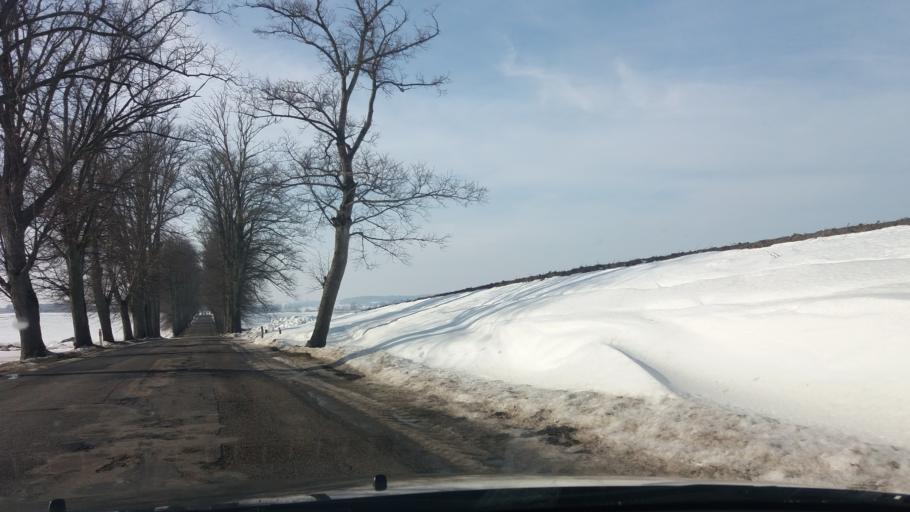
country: PL
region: Warmian-Masurian Voivodeship
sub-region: Powiat bartoszycki
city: Bisztynek
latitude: 54.1121
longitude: 20.8476
